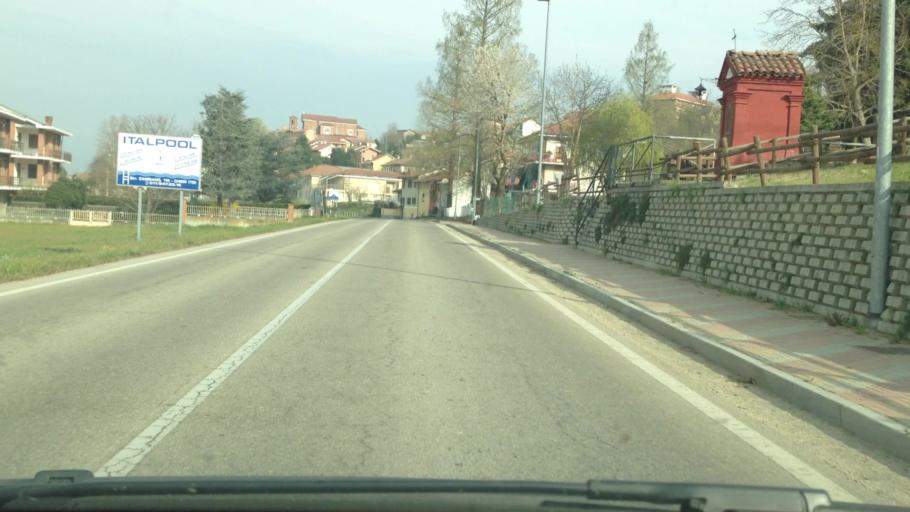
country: IT
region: Piedmont
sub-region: Provincia di Torino
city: Pralormo
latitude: 44.8559
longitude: 7.9062
